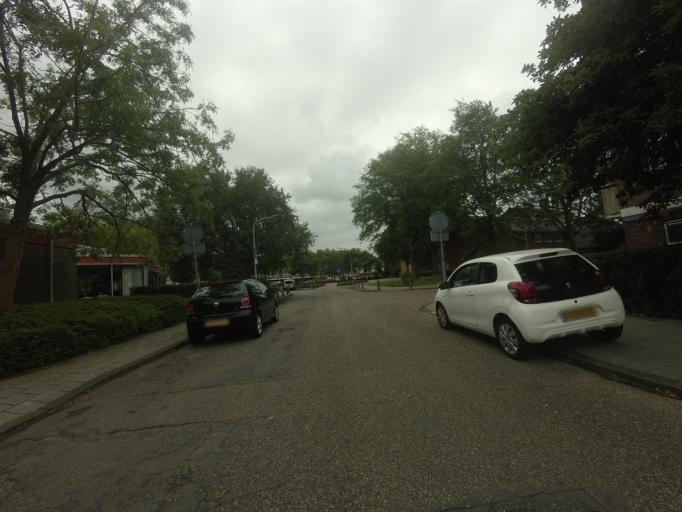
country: NL
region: North Holland
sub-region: Gemeente Bloemendaal
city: Bloemendaal
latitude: 52.4093
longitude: 4.6396
